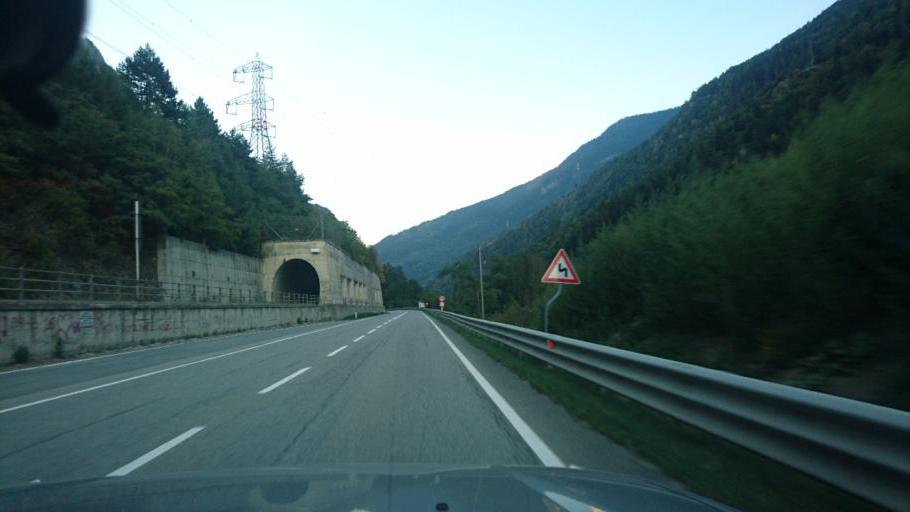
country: IT
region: Aosta Valley
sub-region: Valle d'Aosta
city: Avise
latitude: 45.7190
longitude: 7.1055
